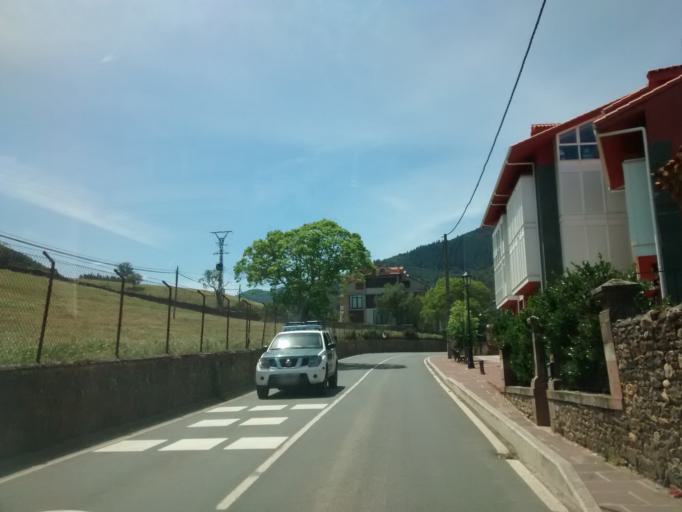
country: ES
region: Cantabria
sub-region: Provincia de Cantabria
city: Potes
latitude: 43.1532
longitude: -4.6215
